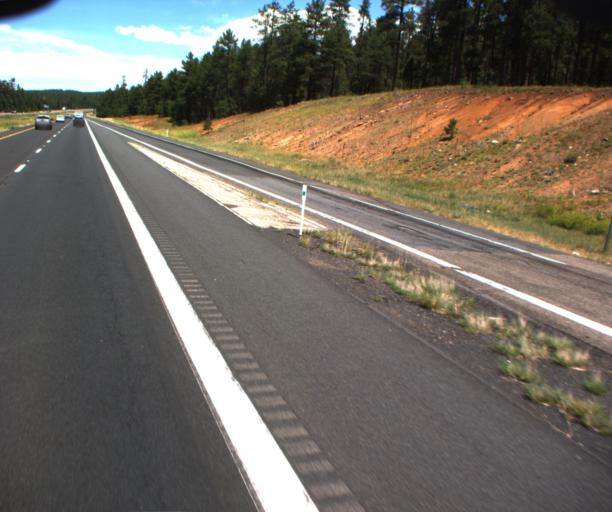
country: US
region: Arizona
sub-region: Coconino County
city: Sedona
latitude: 34.8778
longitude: -111.6365
